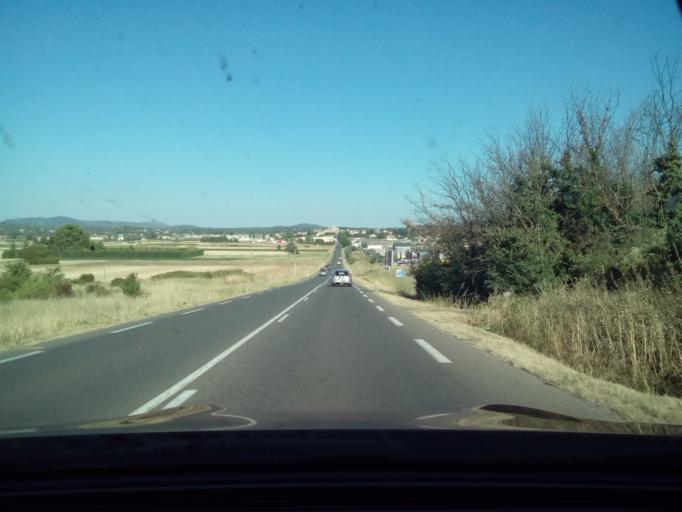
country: FR
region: Provence-Alpes-Cote d'Azur
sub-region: Departement du Var
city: Saint-Maximin-la-Sainte-Baume
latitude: 43.4590
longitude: 5.8340
